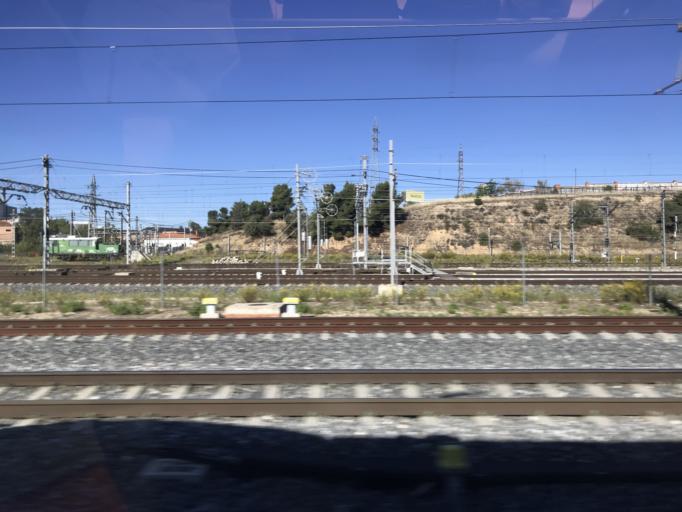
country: ES
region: Madrid
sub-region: Provincia de Madrid
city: Pinar de Chamartin
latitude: 40.4819
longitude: -3.6772
